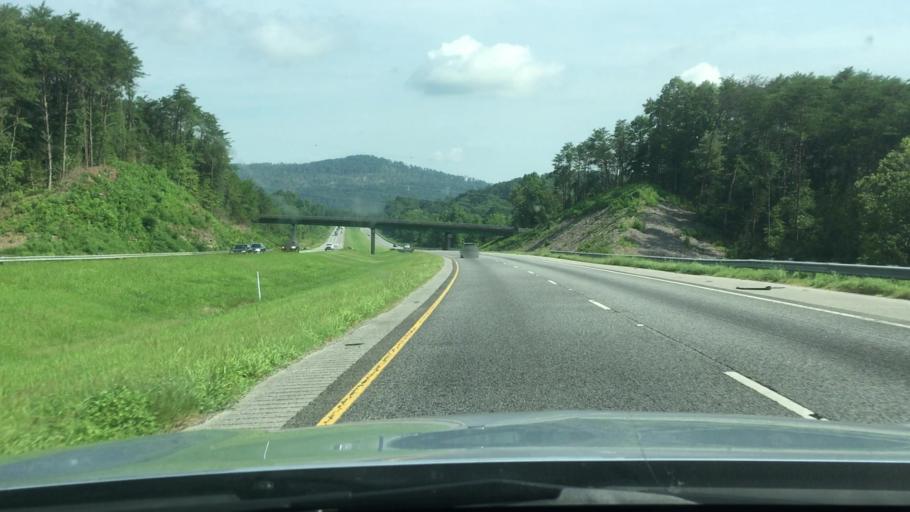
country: US
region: Georgia
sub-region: Dade County
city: Trenton
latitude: 34.9201
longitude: -85.4812
